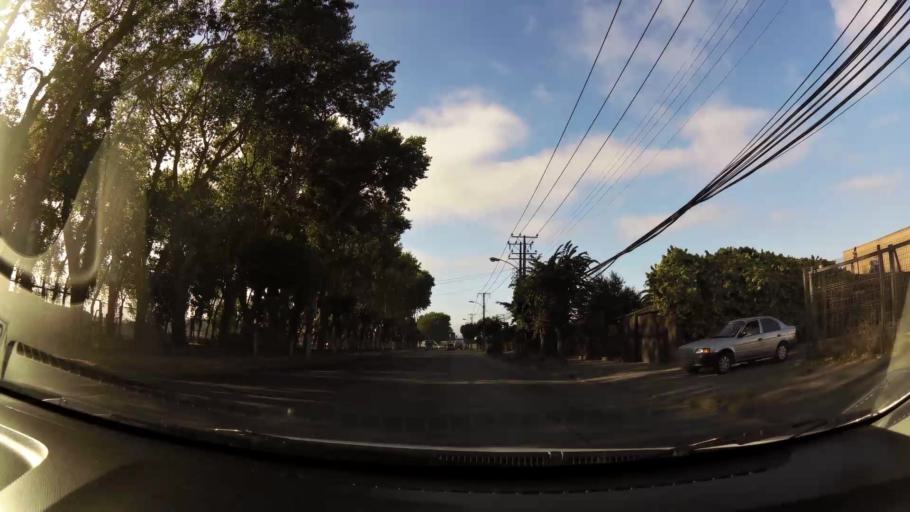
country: CL
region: Biobio
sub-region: Provincia de Concepcion
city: Concepcion
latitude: -36.7857
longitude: -73.0869
